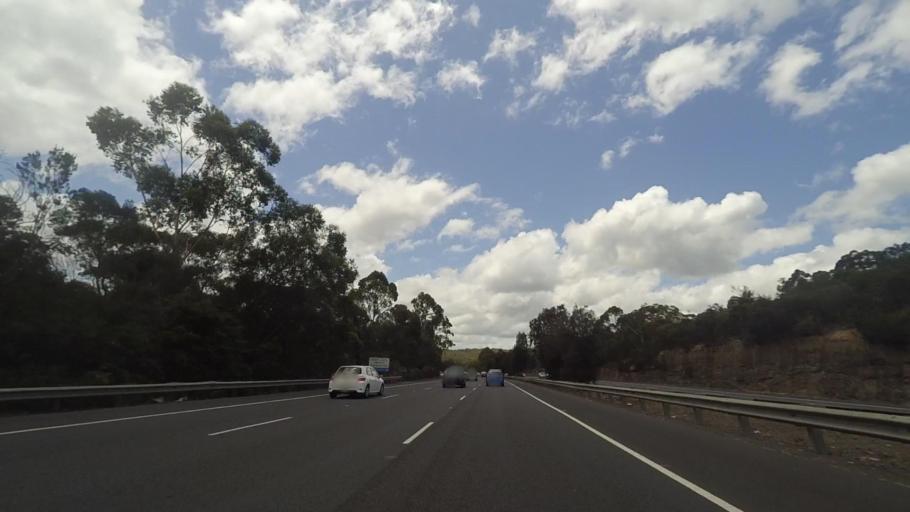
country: AU
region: New South Wales
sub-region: Ku-ring-gai
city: North Wahroonga
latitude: -33.6964
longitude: 151.1202
